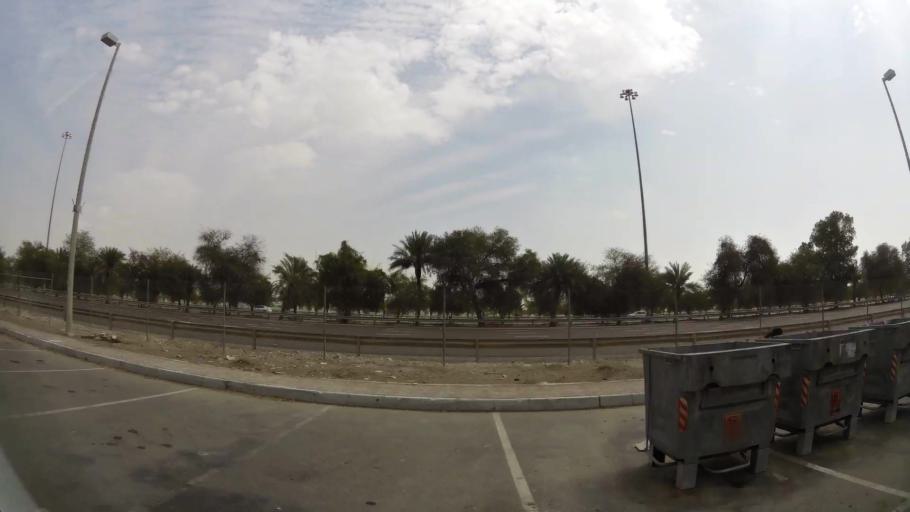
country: AE
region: Abu Dhabi
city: Abu Dhabi
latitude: 24.5243
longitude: 54.6915
